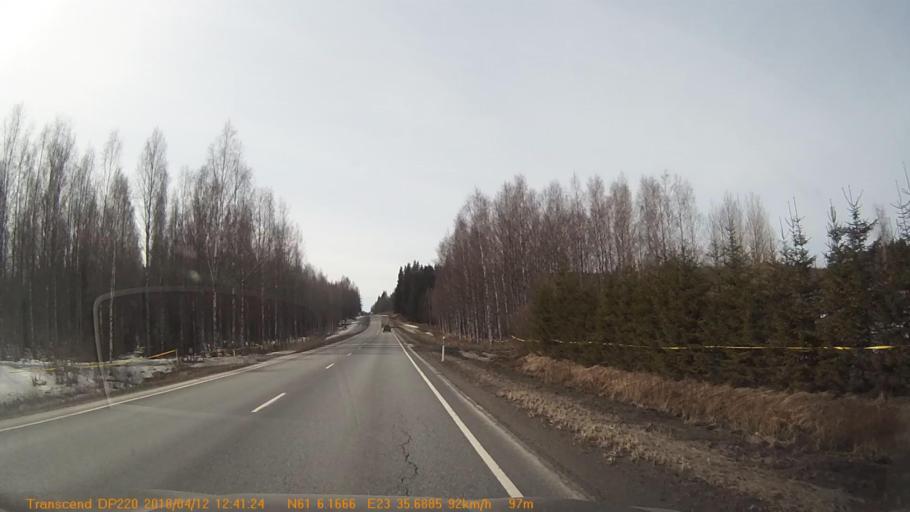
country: FI
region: Pirkanmaa
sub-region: Etelae-Pirkanmaa
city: Urjala
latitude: 61.1027
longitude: 23.5943
